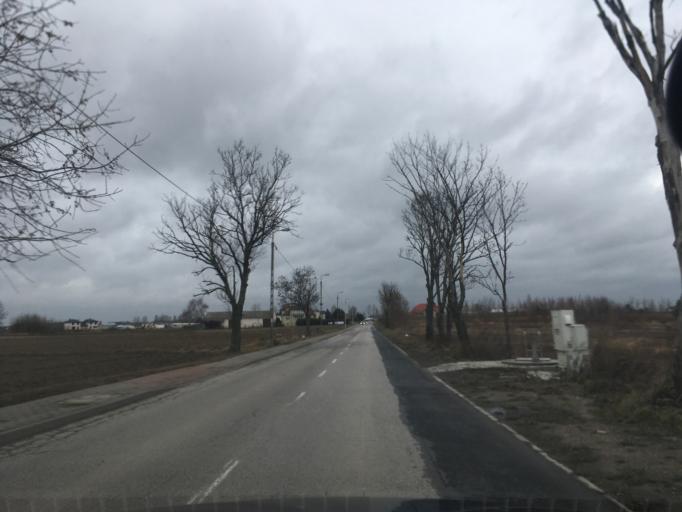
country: PL
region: Masovian Voivodeship
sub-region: Powiat piaseczynski
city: Lesznowola
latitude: 52.1170
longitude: 20.9305
